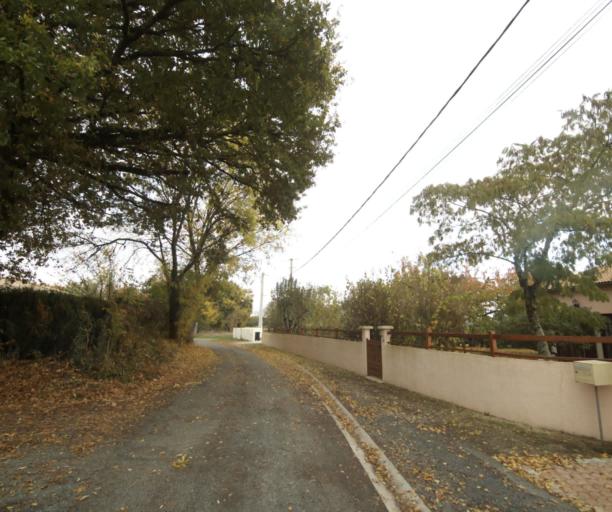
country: FR
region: Poitou-Charentes
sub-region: Departement de la Charente-Maritime
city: Saint-Georges-des-Coteaux
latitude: 45.7873
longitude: -0.7164
